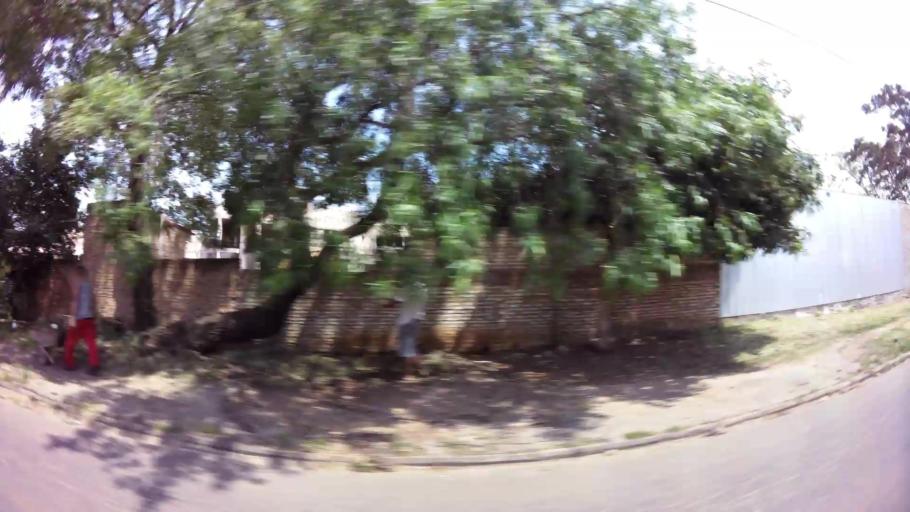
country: PY
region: Asuncion
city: Asuncion
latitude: -25.2808
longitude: -57.5899
